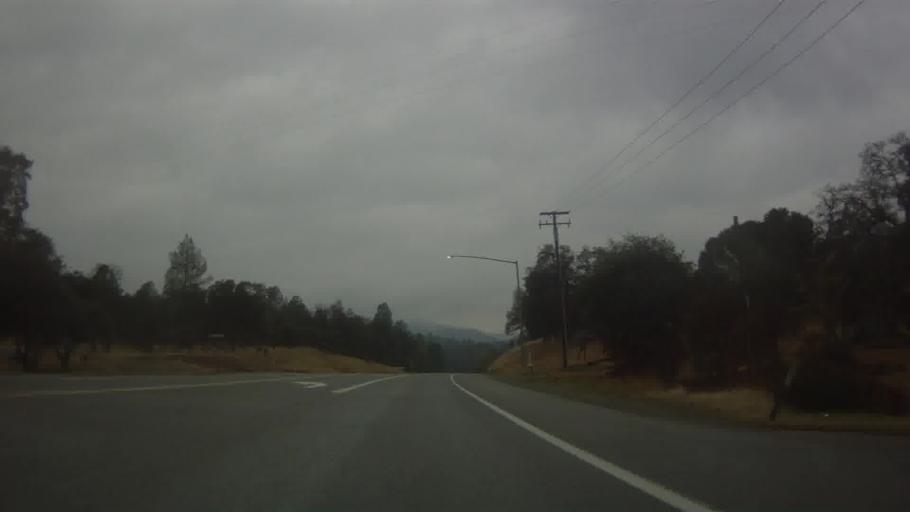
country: US
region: California
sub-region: Shasta County
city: Shasta
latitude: 40.5844
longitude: -122.4461
